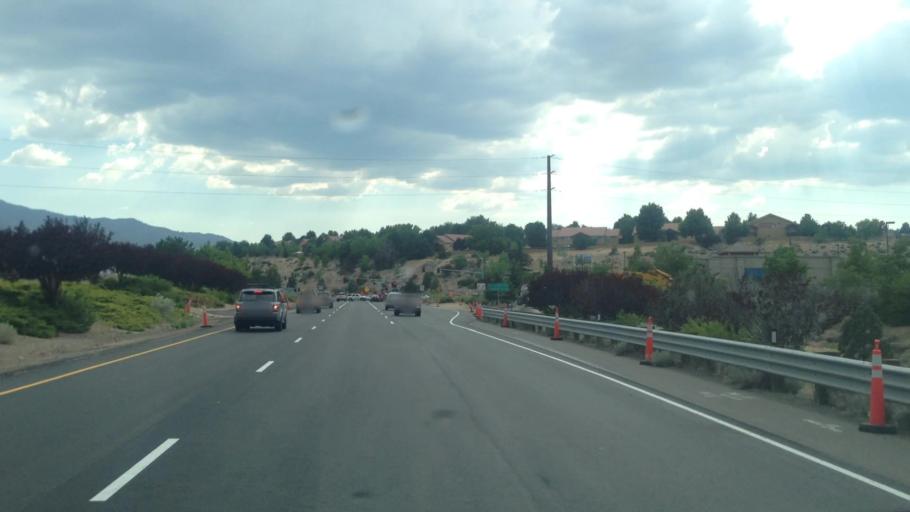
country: US
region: Nevada
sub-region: Washoe County
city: Reno
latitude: 39.5259
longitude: -119.8598
